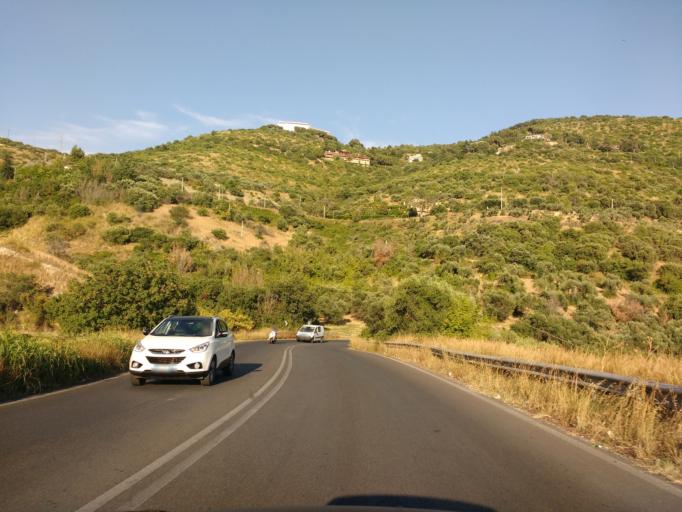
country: IT
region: Latium
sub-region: Citta metropolitana di Roma Capitale
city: Tivoli
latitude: 41.9489
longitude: 12.7921
